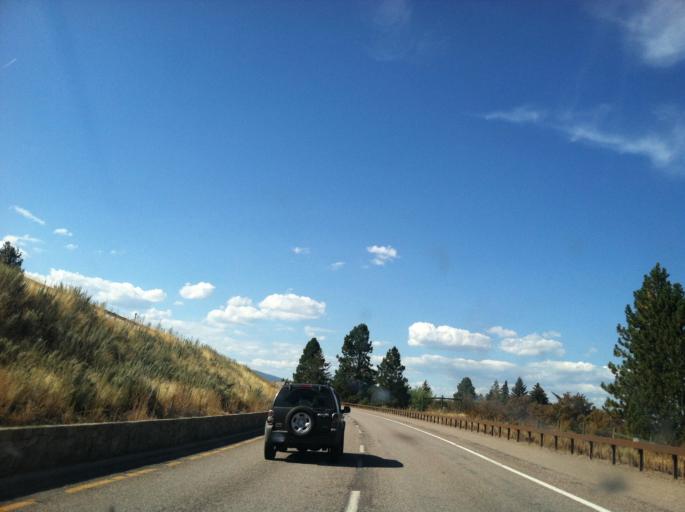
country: US
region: Montana
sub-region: Lake County
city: Polson
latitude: 47.6771
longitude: -114.1090
